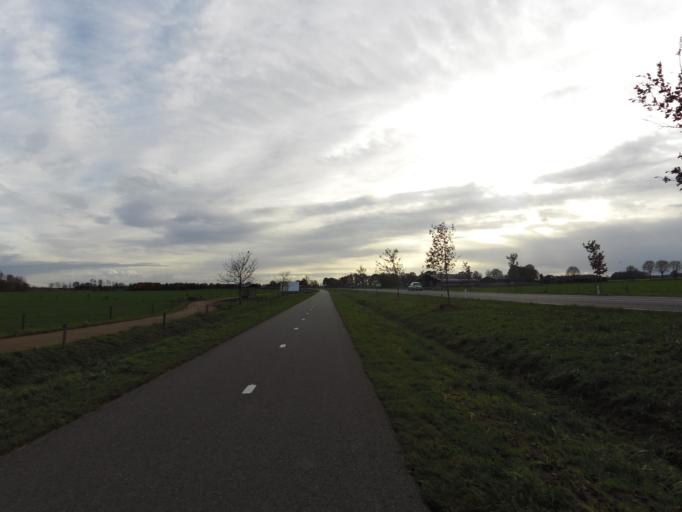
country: NL
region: Gelderland
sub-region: Gemeente Doetinchem
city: Doetinchem
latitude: 51.9342
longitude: 6.3147
